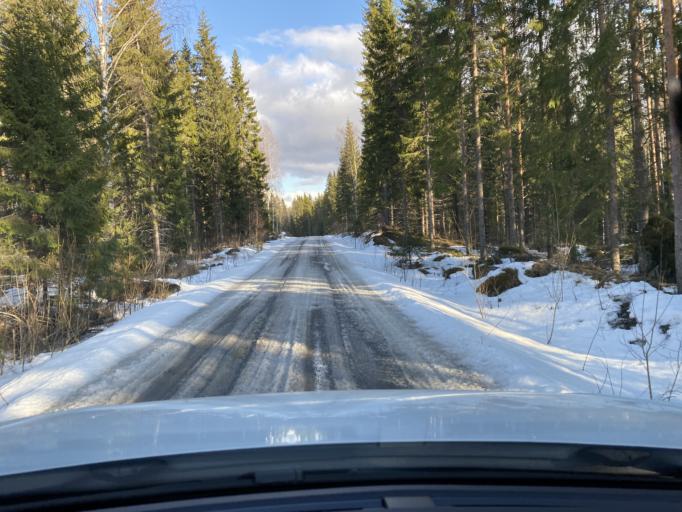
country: FI
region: Pirkanmaa
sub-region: Lounais-Pirkanmaa
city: Mouhijaervi
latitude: 61.4558
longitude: 22.9355
